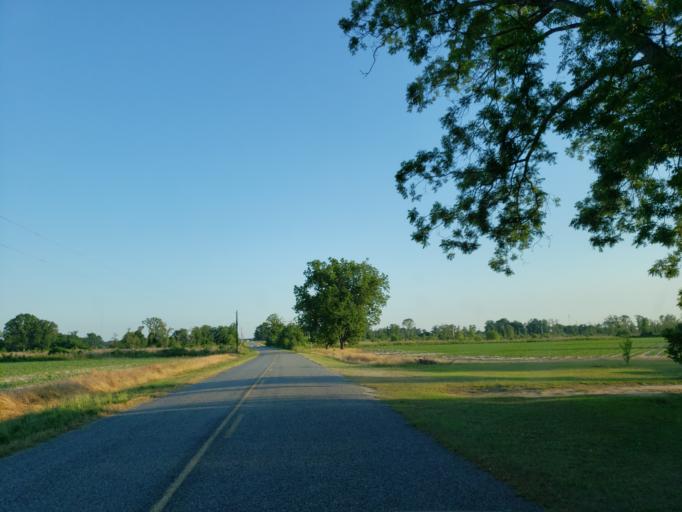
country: US
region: Georgia
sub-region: Dooly County
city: Vienna
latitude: 32.1008
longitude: -83.7563
